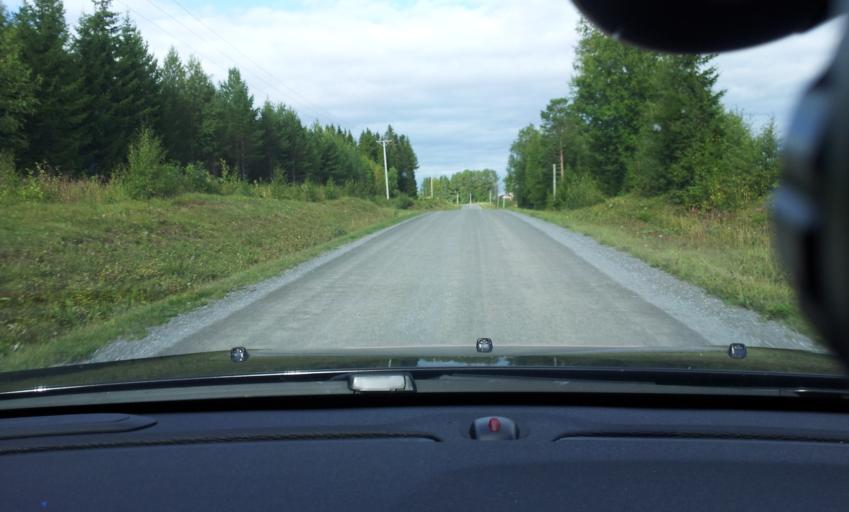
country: SE
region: Jaemtland
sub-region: Krokoms Kommun
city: Valla
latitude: 63.2530
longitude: 13.9510
